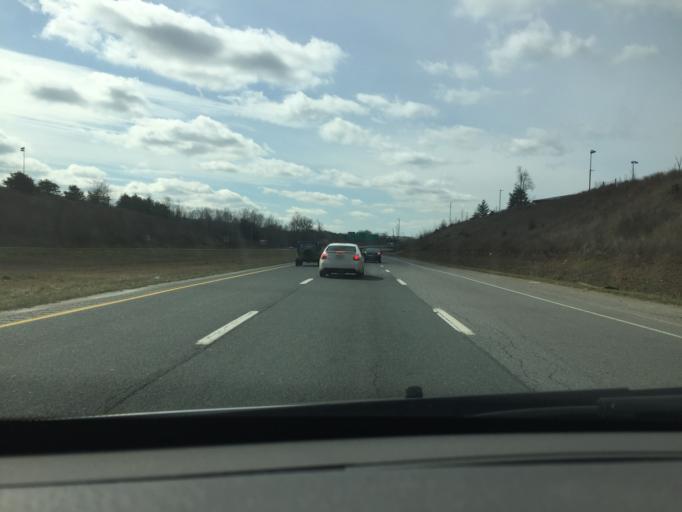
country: US
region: Virginia
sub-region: City of Lynchburg
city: West Lynchburg
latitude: 37.3458
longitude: -79.1818
